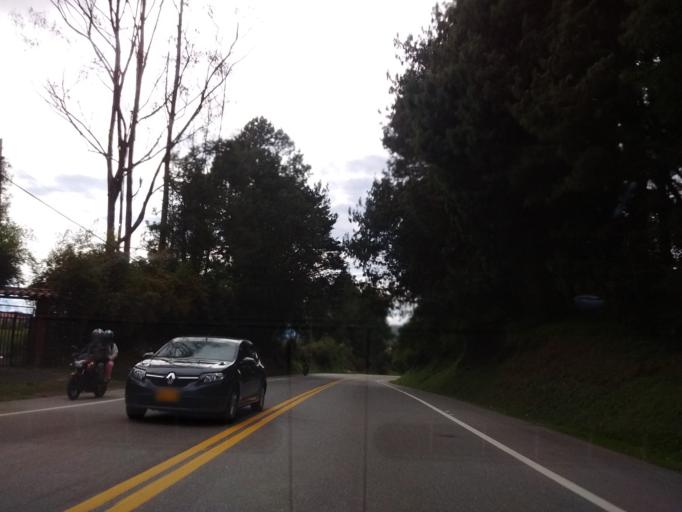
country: CO
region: Antioquia
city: Santuario
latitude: 6.1190
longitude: -75.2343
